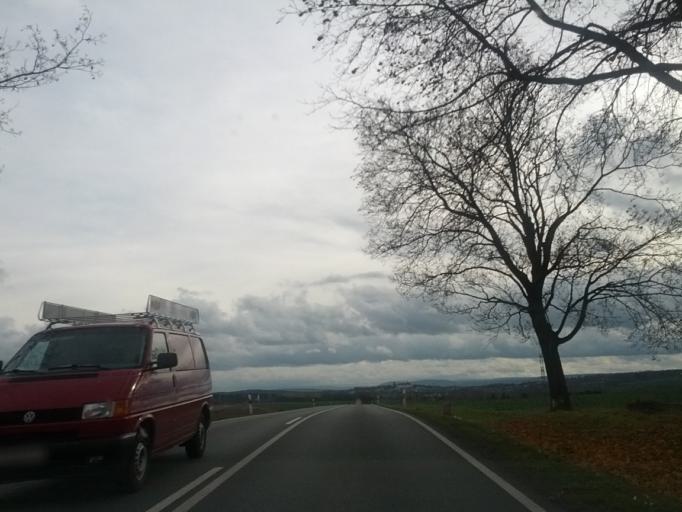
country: DE
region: Thuringia
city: Remstadt
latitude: 50.9880
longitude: 10.6920
